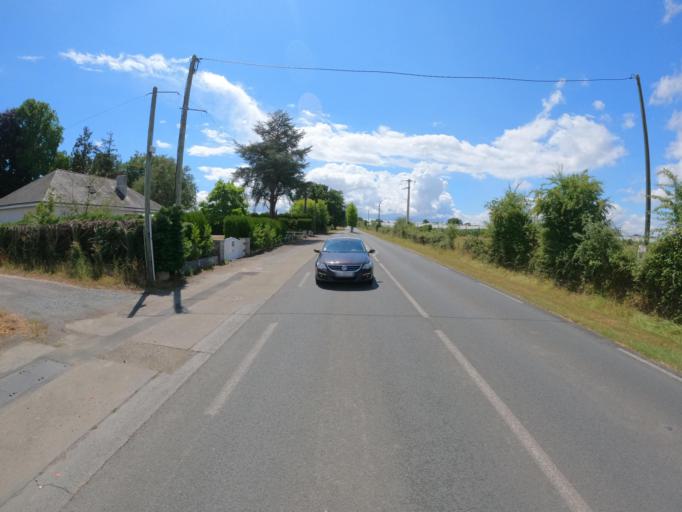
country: FR
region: Pays de la Loire
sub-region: Departement de Maine-et-Loire
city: Champigne
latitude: 47.6581
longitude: -0.5743
